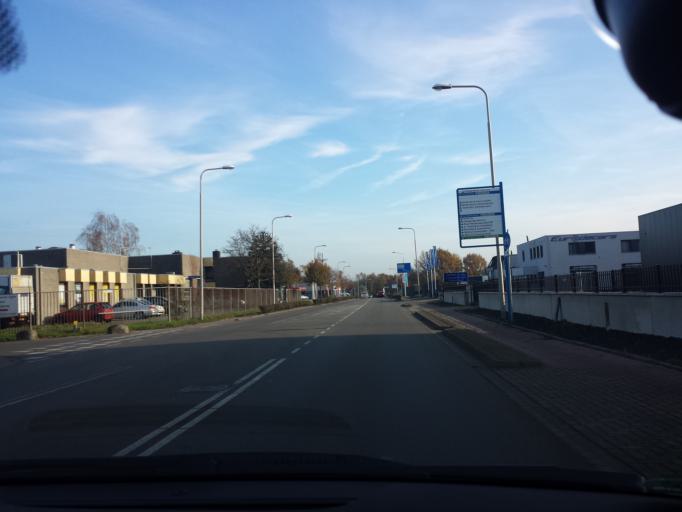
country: NL
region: Limburg
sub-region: Gemeente Kerkrade
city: Kerkrade
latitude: 50.8714
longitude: 6.0386
